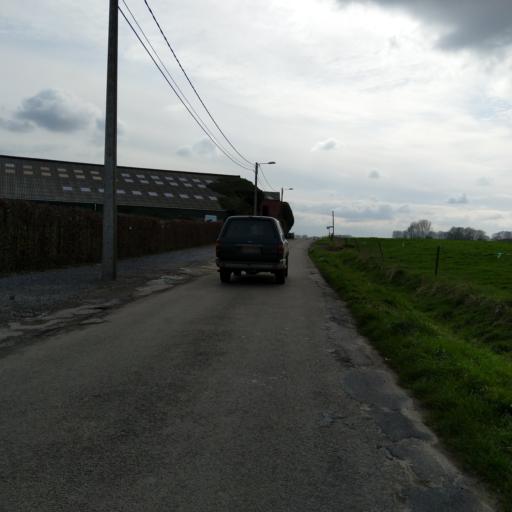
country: BE
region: Wallonia
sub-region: Province du Hainaut
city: Soignies
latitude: 50.5599
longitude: 4.0640
